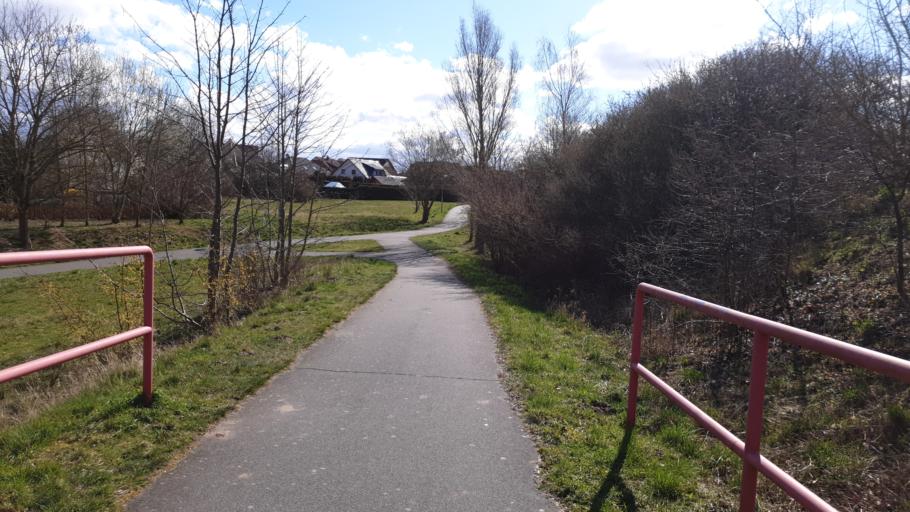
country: DE
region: Mecklenburg-Vorpommern
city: Lankow
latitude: 53.6401
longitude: 11.3522
